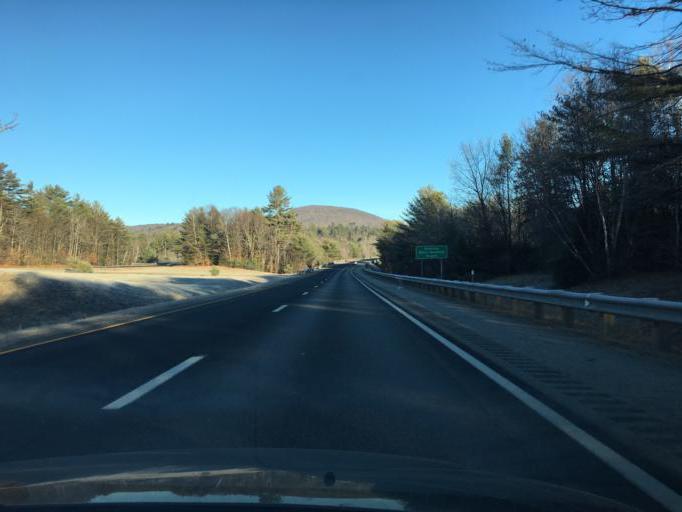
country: US
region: New Hampshire
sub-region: Grafton County
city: Plymouth
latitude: 43.7958
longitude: -71.6757
